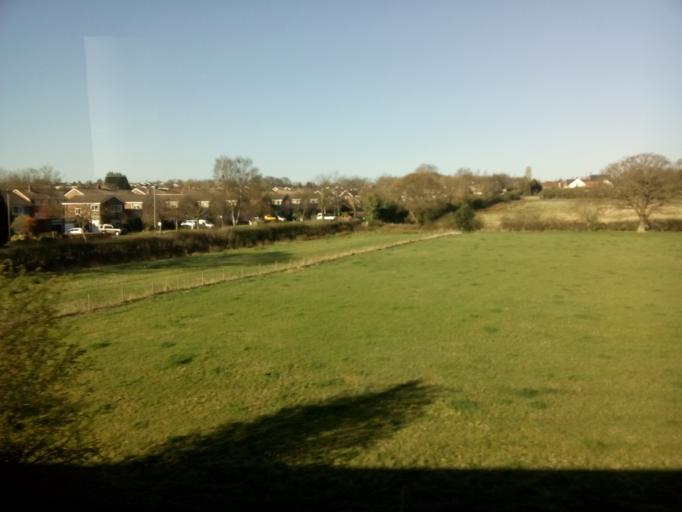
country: GB
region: England
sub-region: County Durham
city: Durham
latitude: 54.8062
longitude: -1.5636
